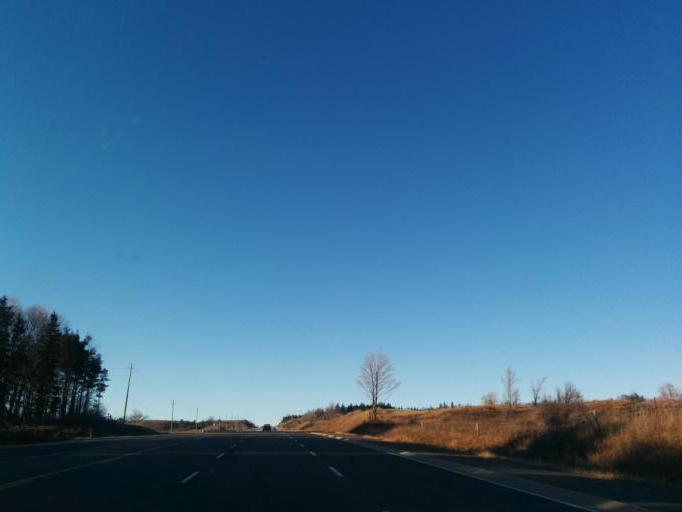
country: CA
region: Ontario
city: Orangeville
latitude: 43.8356
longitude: -79.9624
